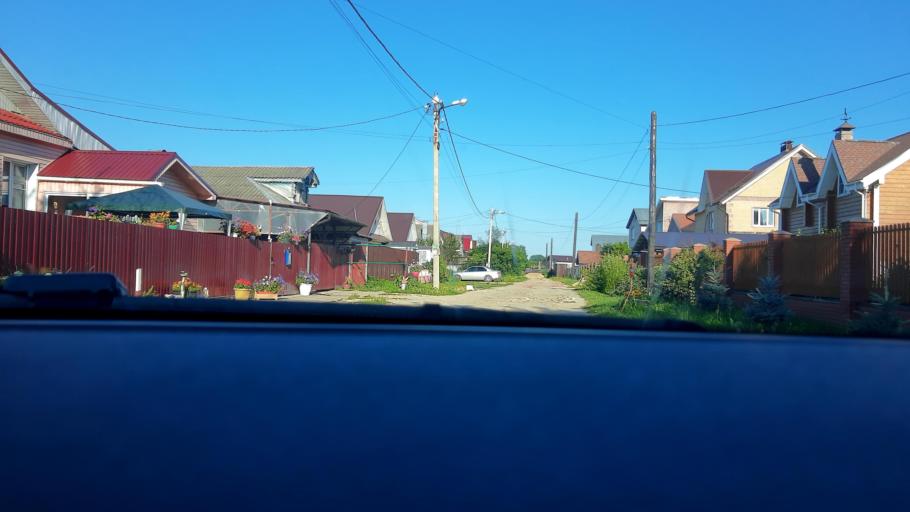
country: RU
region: Nizjnij Novgorod
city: Neklyudovo
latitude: 56.4060
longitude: 44.0343
